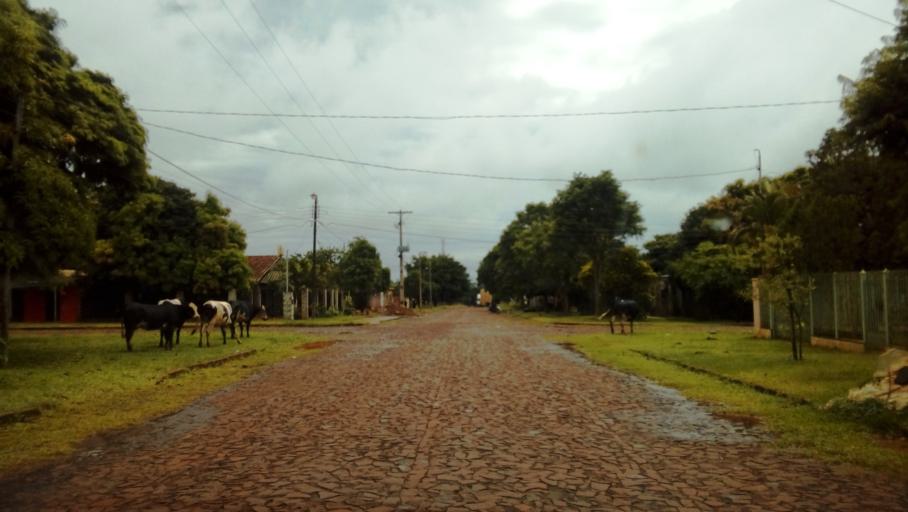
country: PY
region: Alto Parana
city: Ciudad del Este
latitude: -25.4269
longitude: -54.6430
